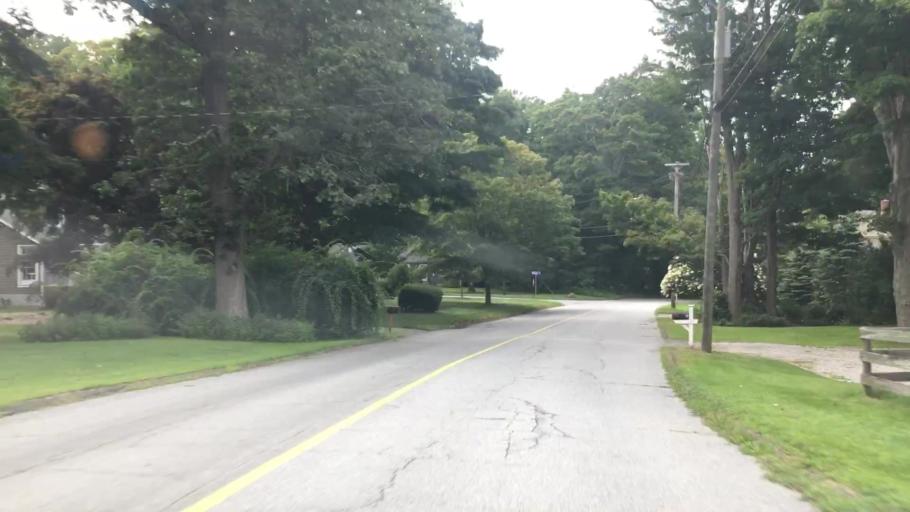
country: US
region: Connecticut
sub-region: Middlesex County
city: Deep River Center
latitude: 41.3388
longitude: -72.4413
